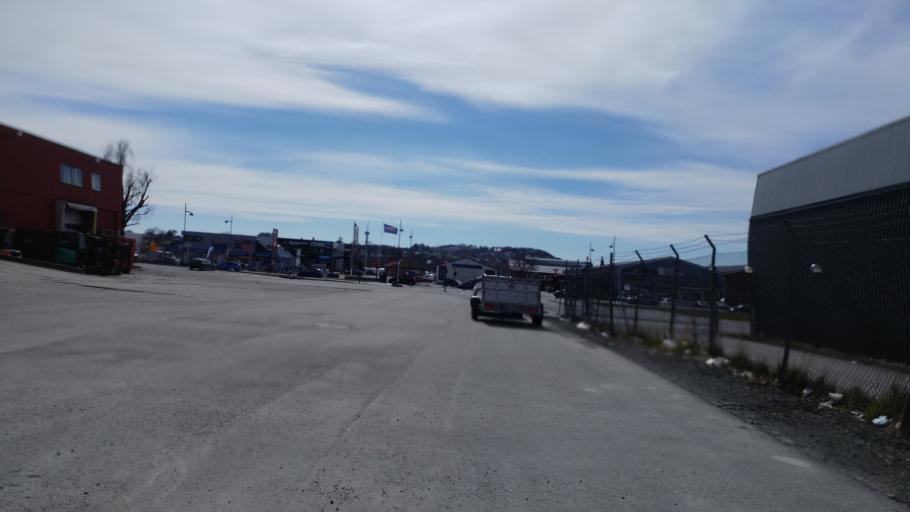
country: NO
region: Sor-Trondelag
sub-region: Trondheim
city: Trondheim
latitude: 63.4430
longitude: 10.4553
